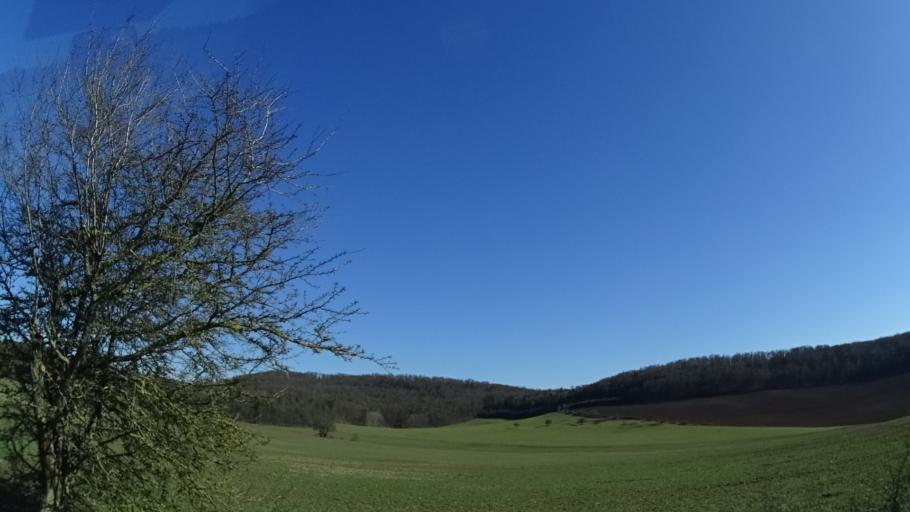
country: DE
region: Bavaria
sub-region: Regierungsbezirk Unterfranken
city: Willmars
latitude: 50.4923
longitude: 10.2867
